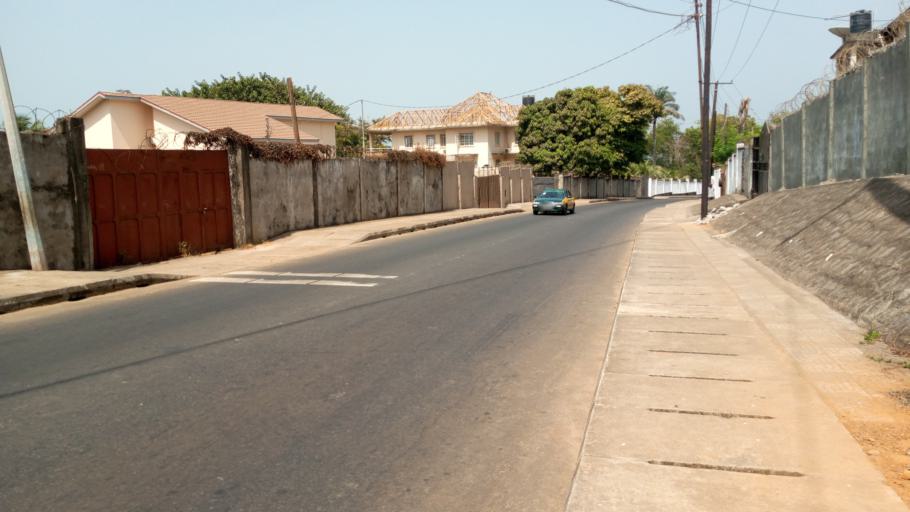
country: SL
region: Western Area
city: Freetown
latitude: 8.4826
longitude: -13.2616
